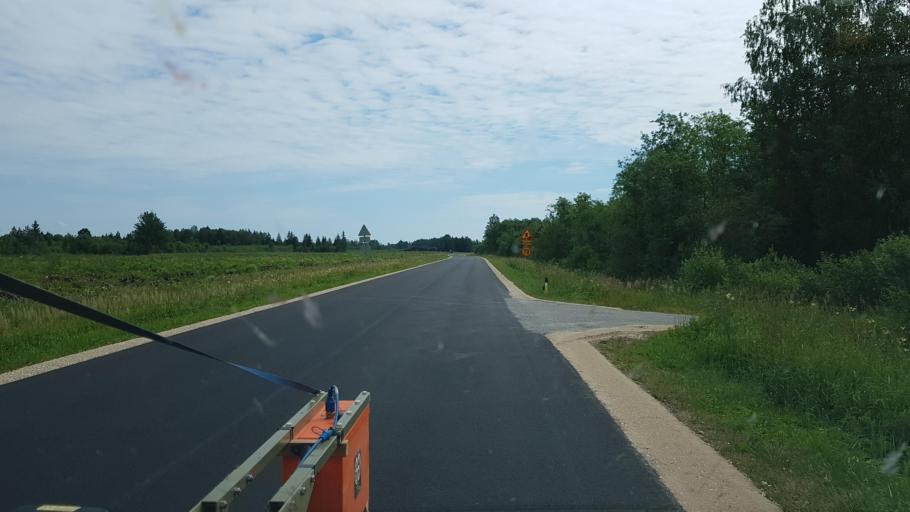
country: EE
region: Paernumaa
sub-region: Halinga vald
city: Parnu-Jaagupi
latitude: 58.6197
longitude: 24.2756
